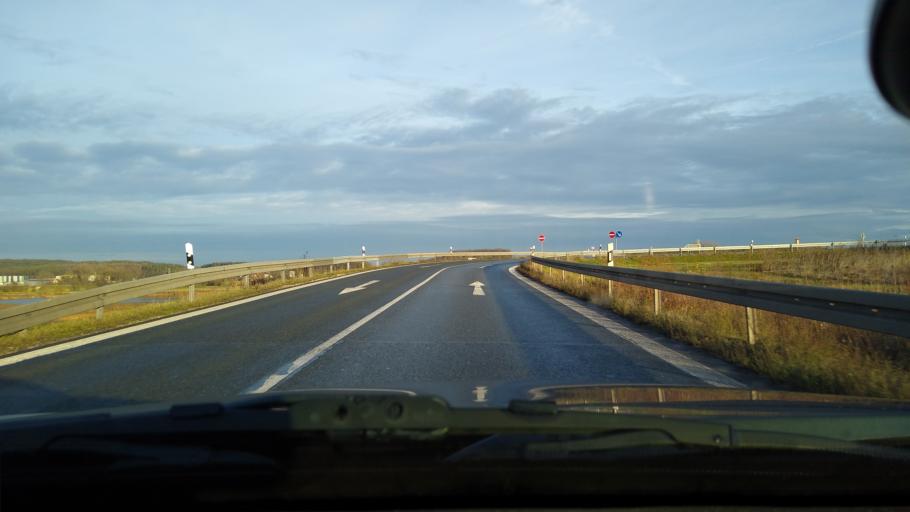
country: DE
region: Bavaria
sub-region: Regierungsbezirk Mittelfranken
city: Gremsdorf
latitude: 49.6997
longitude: 10.8538
